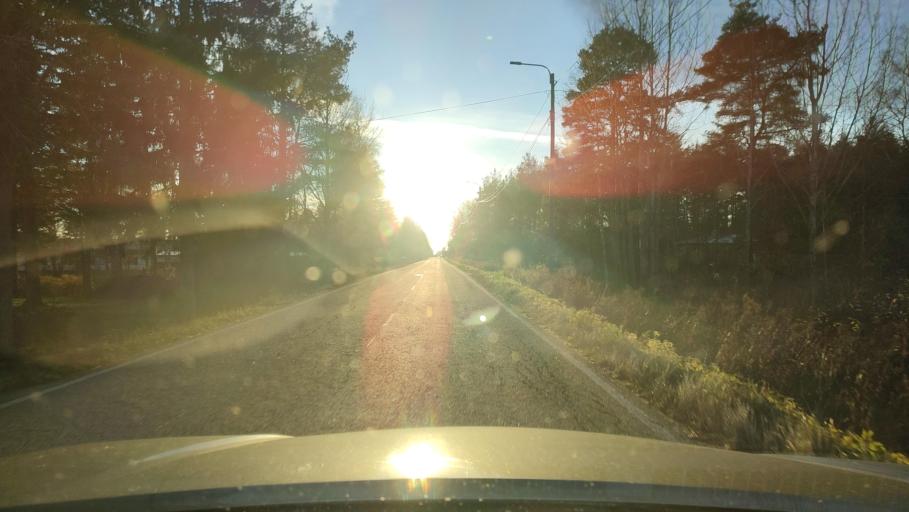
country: FI
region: Ostrobothnia
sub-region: Vaasa
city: Malax
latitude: 62.7069
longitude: 21.6016
